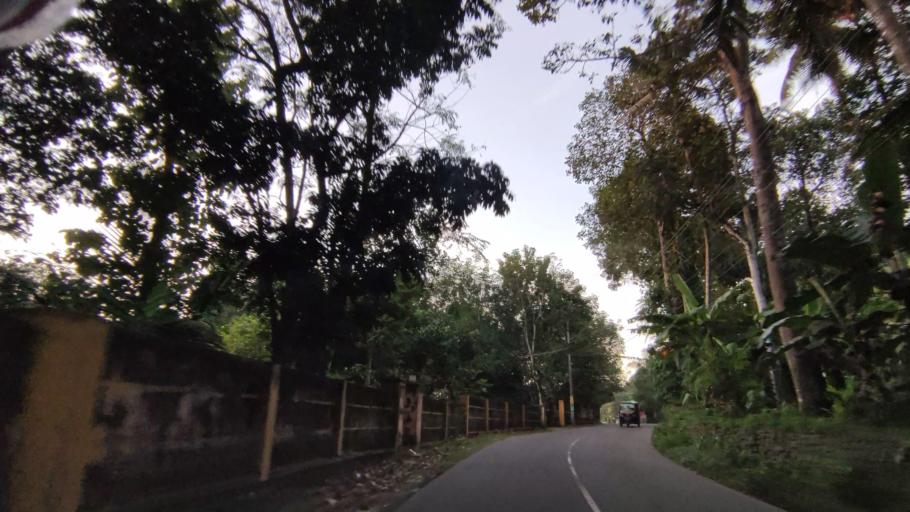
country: IN
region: Kerala
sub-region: Kottayam
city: Kottayam
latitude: 9.6488
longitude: 76.5097
